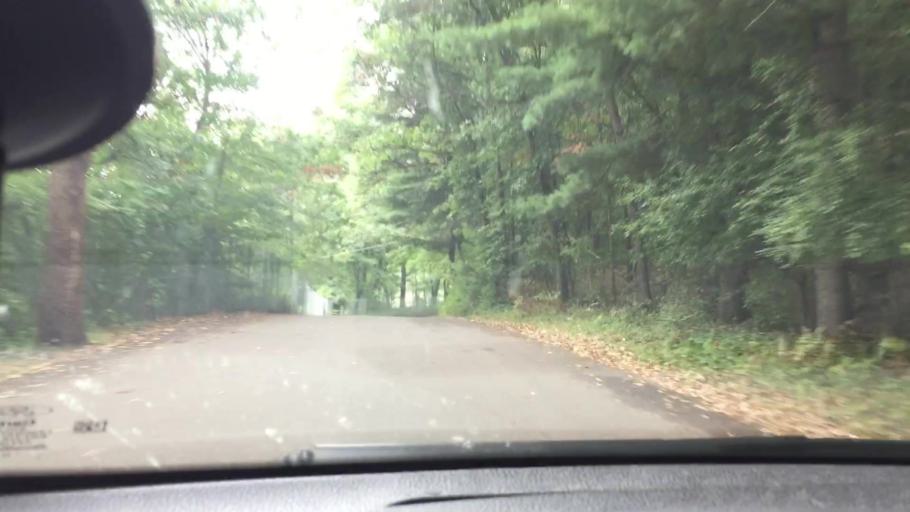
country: US
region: Wisconsin
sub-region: Chippewa County
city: Chippewa Falls
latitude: 44.9510
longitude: -91.4000
